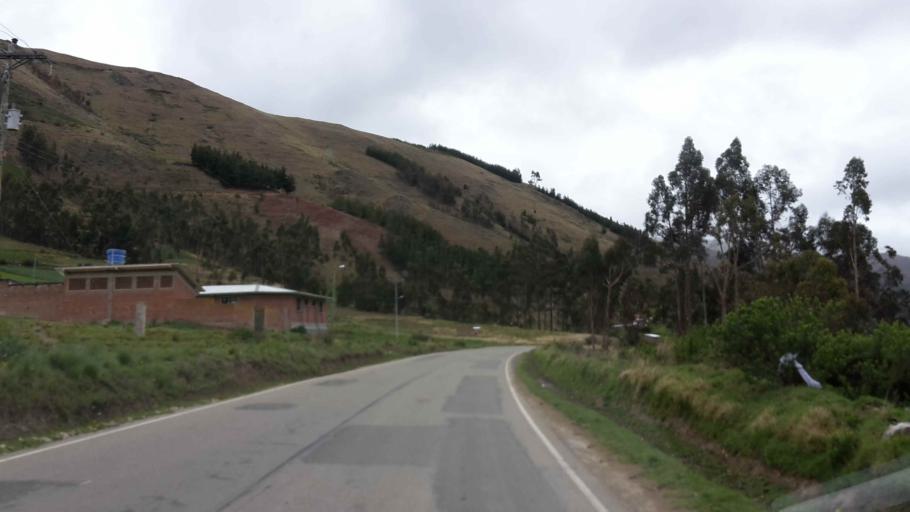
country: BO
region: Cochabamba
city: Arani
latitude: -17.4802
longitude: -65.5447
